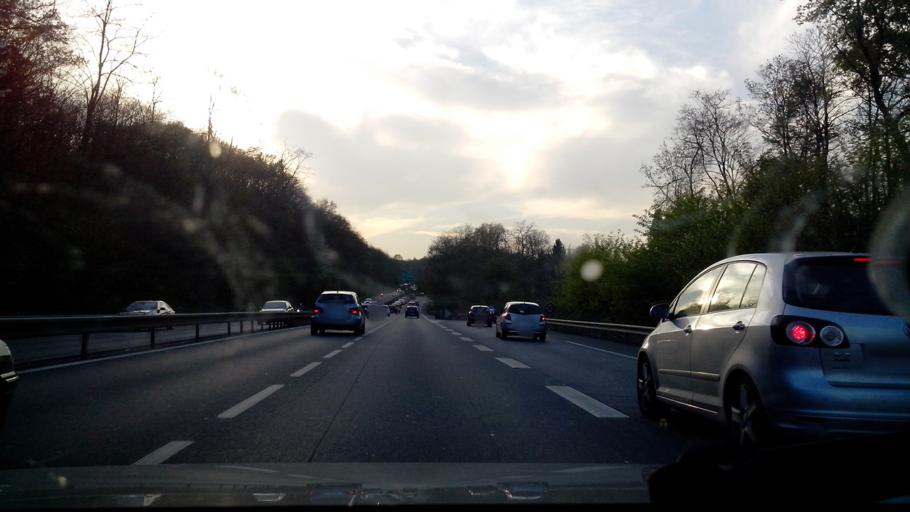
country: FR
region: Ile-de-France
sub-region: Departement de l'Essonne
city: Bievres
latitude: 48.7492
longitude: 2.2120
